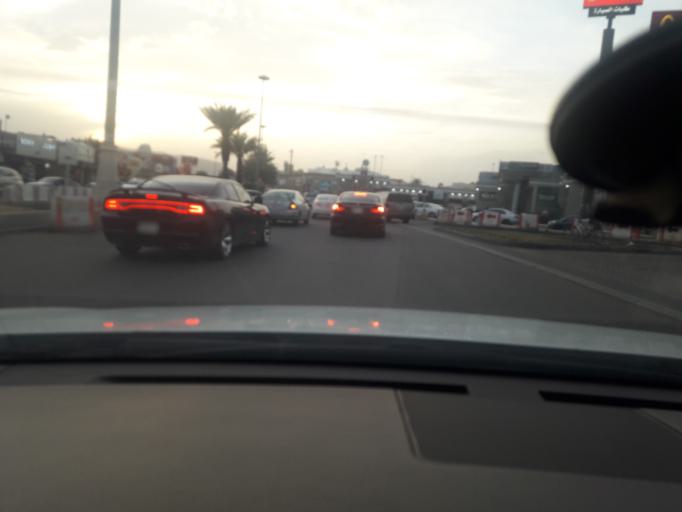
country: SA
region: Al Madinah al Munawwarah
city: Sultanah
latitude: 24.4891
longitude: 39.5827
